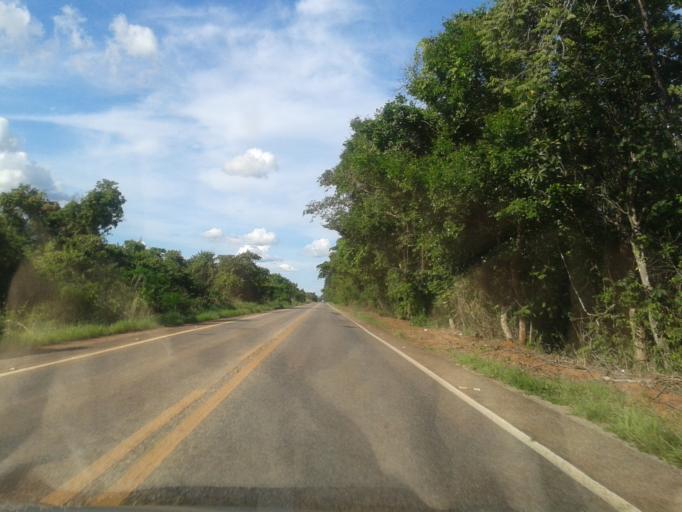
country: BR
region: Goias
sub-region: Mozarlandia
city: Mozarlandia
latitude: -14.4420
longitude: -50.4590
